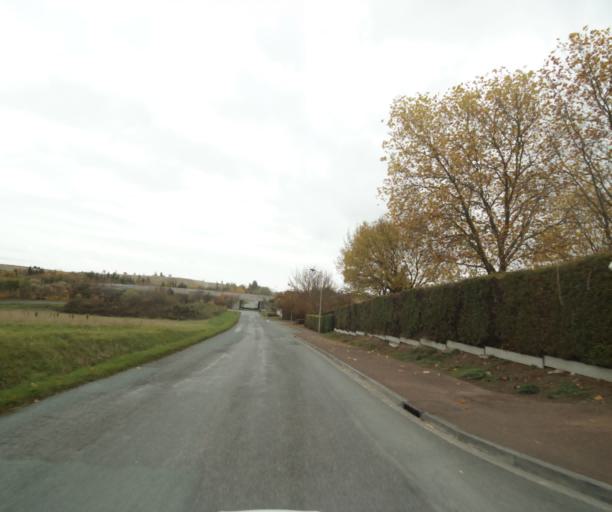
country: FR
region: Poitou-Charentes
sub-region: Departement de la Charente-Maritime
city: Saintes
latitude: 45.7282
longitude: -0.6512
